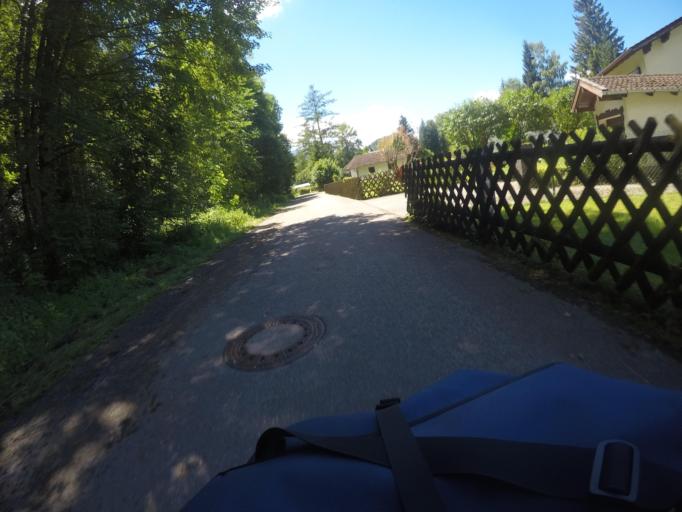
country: DE
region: Bavaria
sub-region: Swabia
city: Schwangau
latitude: 47.5589
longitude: 10.7461
